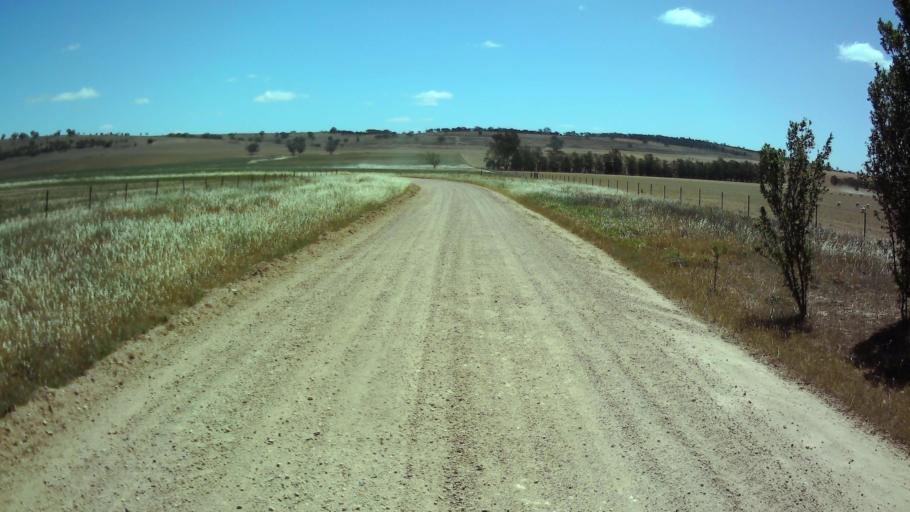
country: AU
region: New South Wales
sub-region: Weddin
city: Grenfell
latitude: -33.9333
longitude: 148.3313
